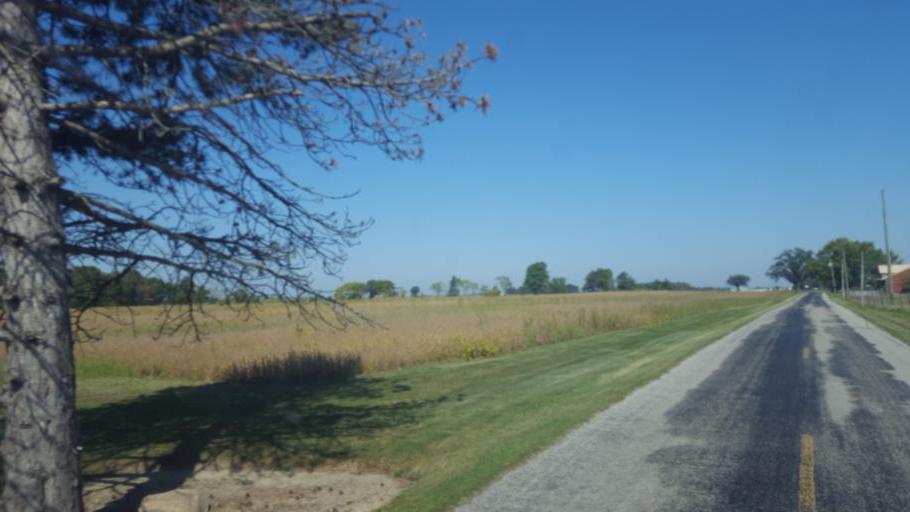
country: US
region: Ohio
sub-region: Union County
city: Richwood
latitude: 40.5095
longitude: -83.4374
